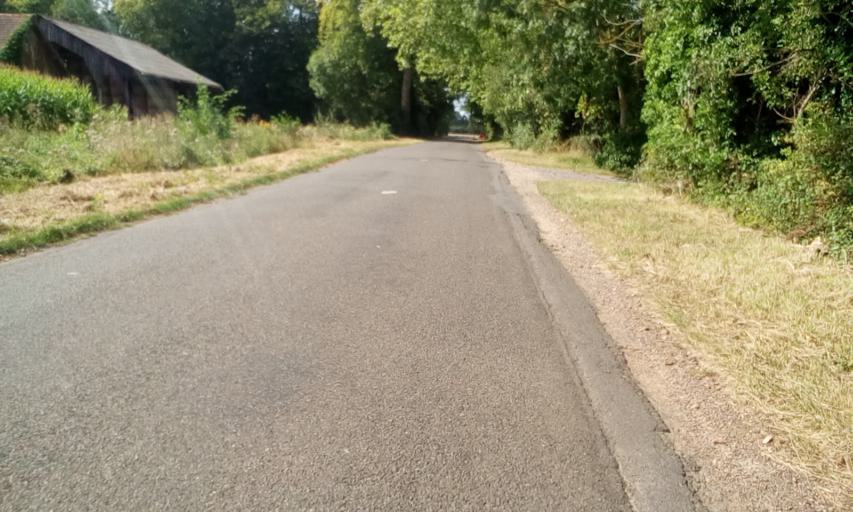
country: FR
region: Lower Normandy
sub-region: Departement du Calvados
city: Bellengreville
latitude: 49.1435
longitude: -0.2136
